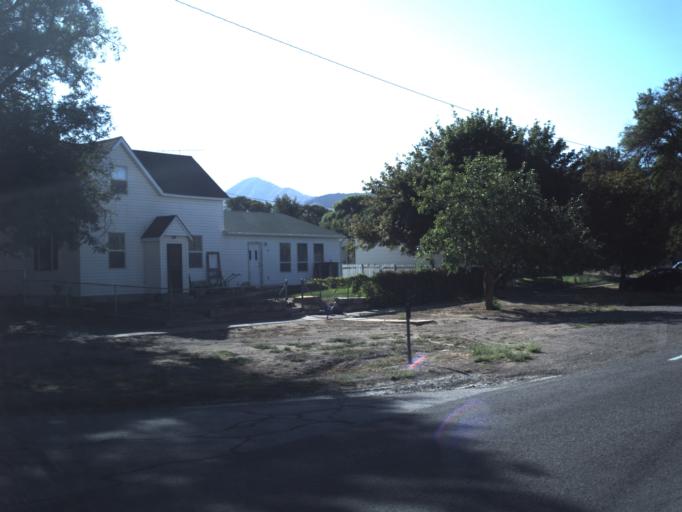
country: US
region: Utah
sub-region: Millard County
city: Delta
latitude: 39.3750
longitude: -112.3361
